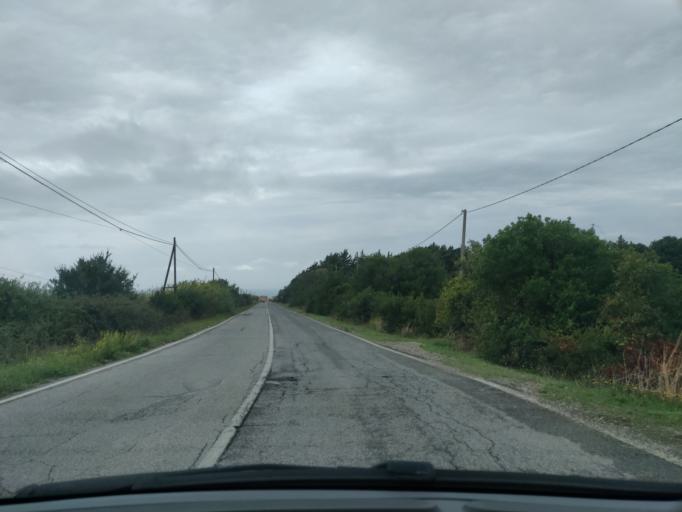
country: IT
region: Latium
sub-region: Citta metropolitana di Roma Capitale
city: Civitavecchia
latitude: 42.1095
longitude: 11.8415
